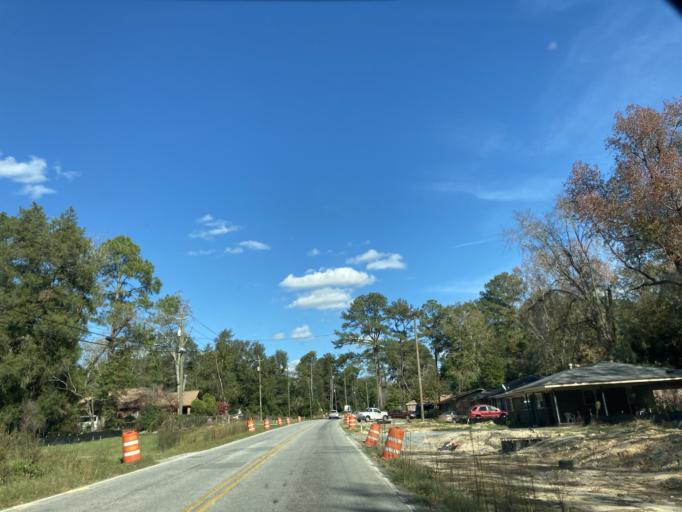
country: US
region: Georgia
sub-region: Bibb County
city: Macon
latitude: 32.8561
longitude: -83.5861
